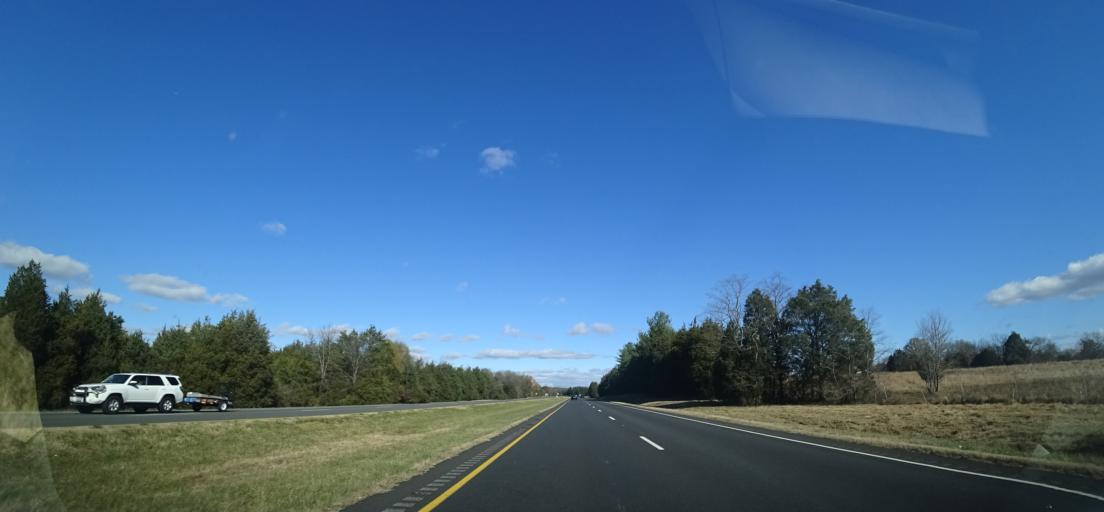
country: US
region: Virginia
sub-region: Fauquier County
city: Bealeton
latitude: 38.5534
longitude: -77.8048
